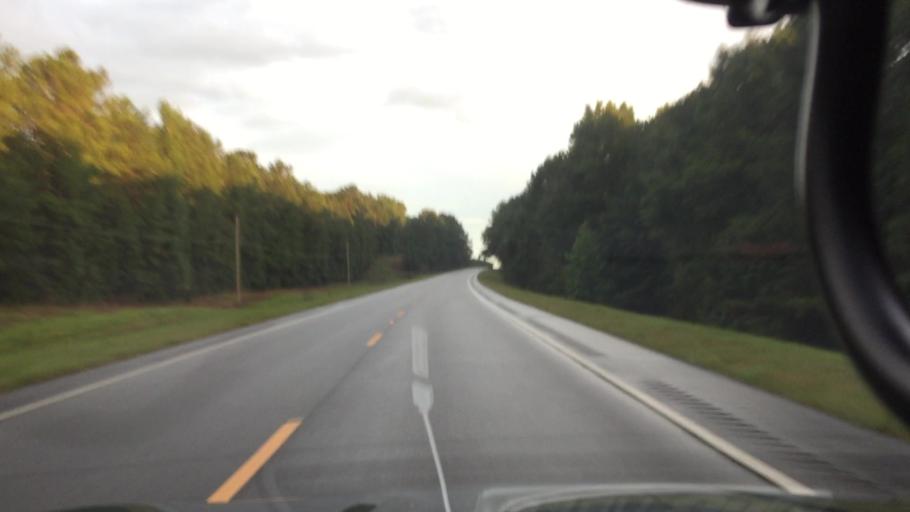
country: US
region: Alabama
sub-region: Coffee County
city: New Brockton
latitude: 31.5534
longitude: -85.9208
